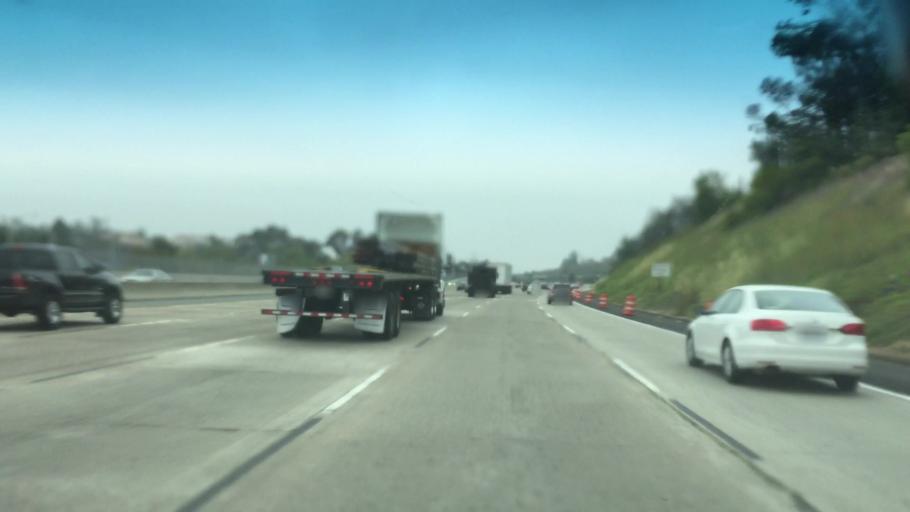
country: US
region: California
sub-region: San Diego County
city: La Mesa
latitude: 32.7780
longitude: -117.0576
